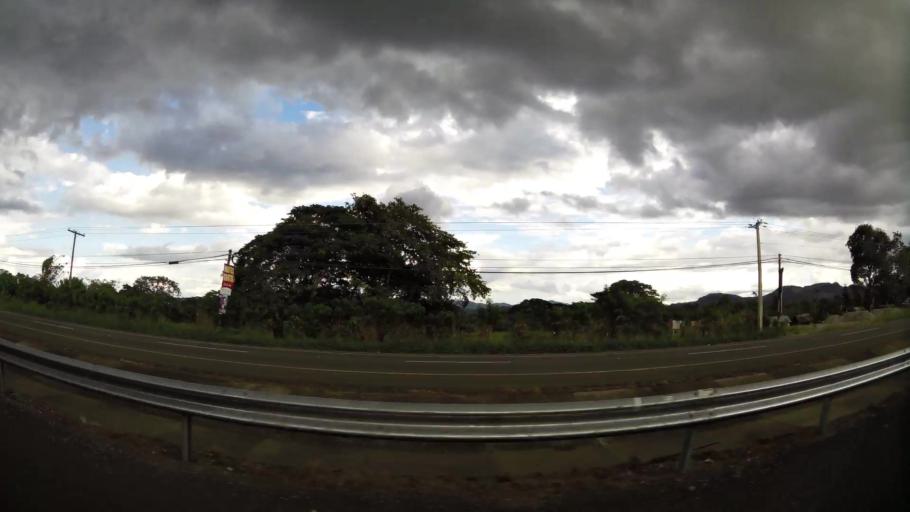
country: DO
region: Monsenor Nouel
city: Sabana del Puerto
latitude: 19.0152
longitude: -70.4449
